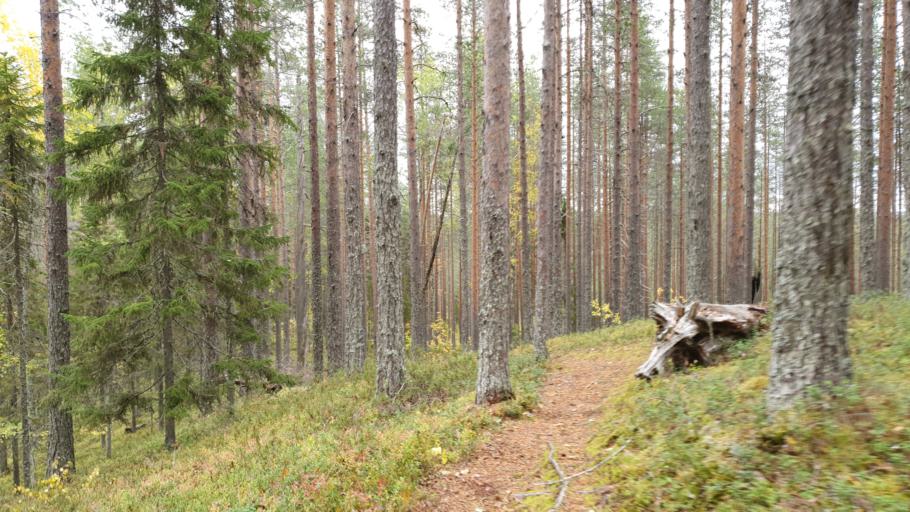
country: FI
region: Kainuu
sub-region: Kehys-Kainuu
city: Kuhmo
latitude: 64.2921
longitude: 29.3289
